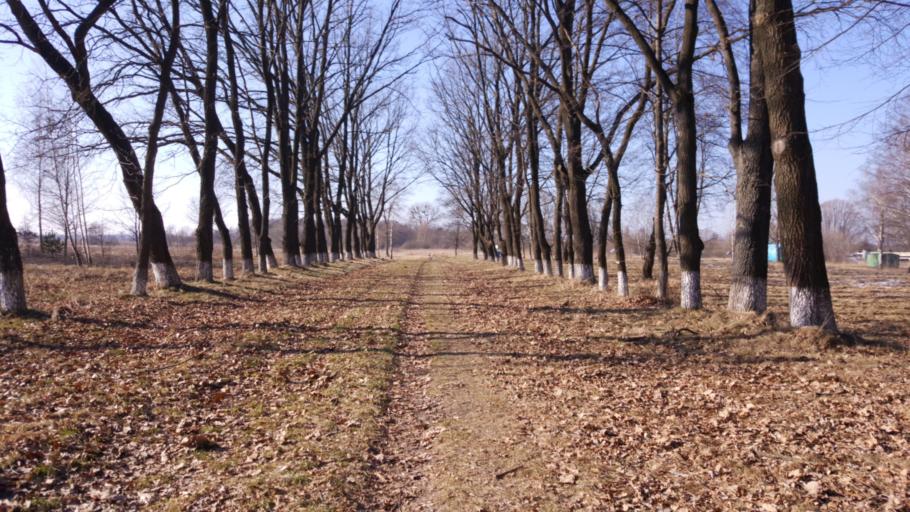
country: BY
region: Brest
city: Kamyanyets
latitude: 52.4007
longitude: 23.8057
